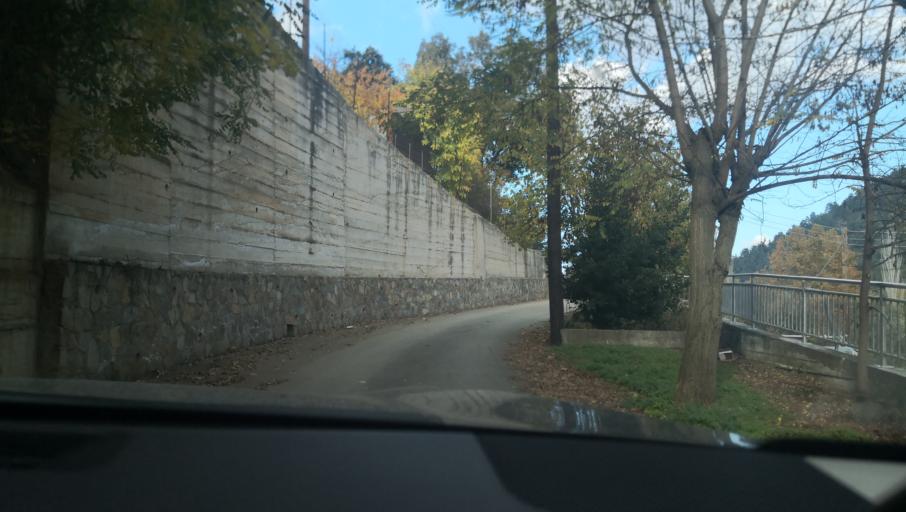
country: CY
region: Lefkosia
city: Lefka
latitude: 35.0392
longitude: 32.7321
